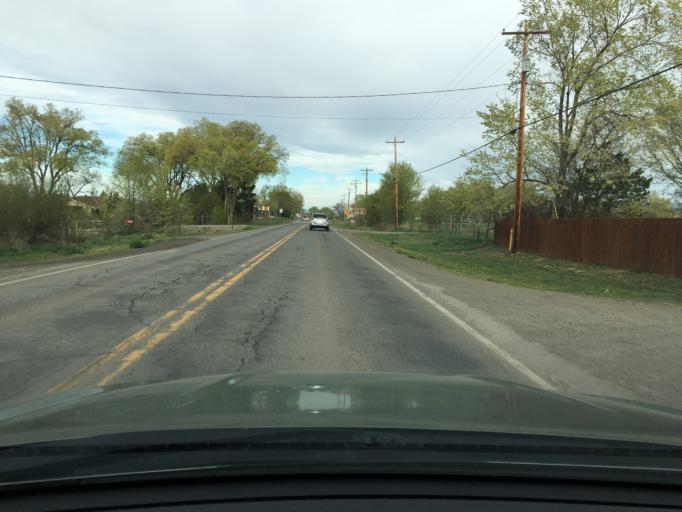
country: US
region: Colorado
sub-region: Delta County
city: Cedaredge
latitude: 38.8004
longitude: -107.7774
